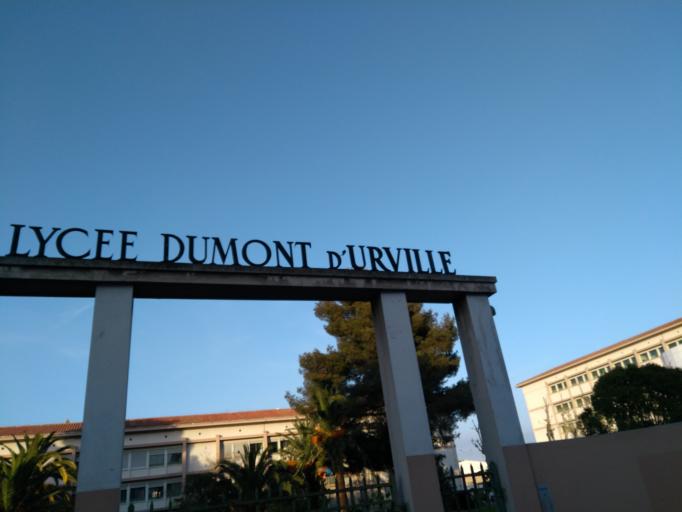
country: FR
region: Provence-Alpes-Cote d'Azur
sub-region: Departement du Var
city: Toulon
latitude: 43.1158
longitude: 5.9380
